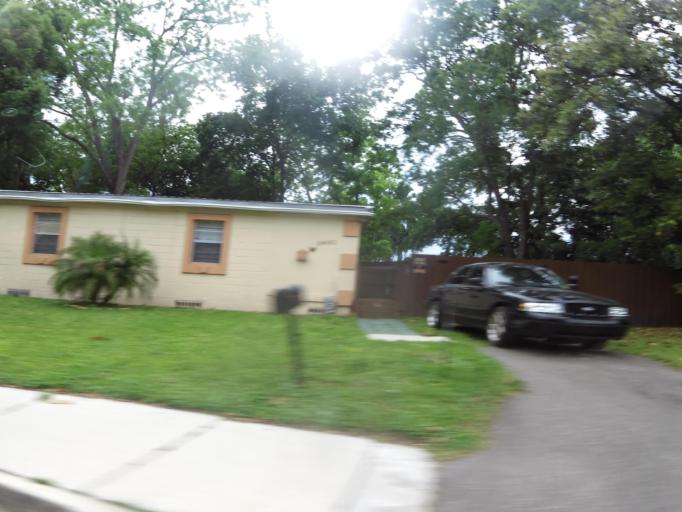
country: US
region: Florida
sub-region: Duval County
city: Jacksonville
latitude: 30.3076
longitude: -81.7410
